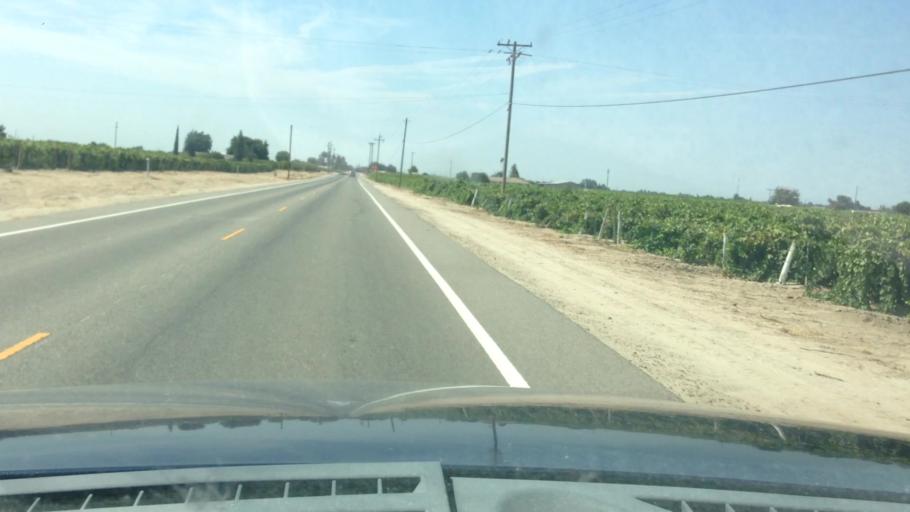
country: US
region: California
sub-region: Fresno County
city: Kingsburg
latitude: 36.5647
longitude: -119.5567
